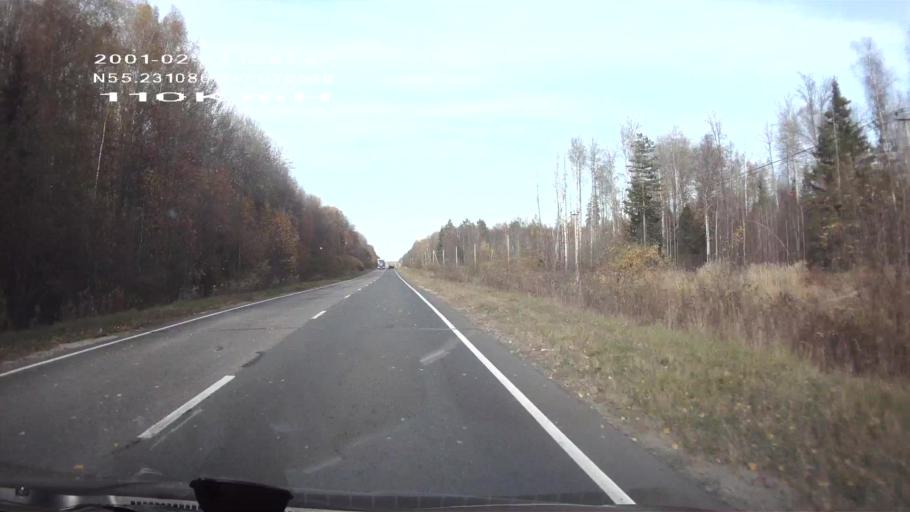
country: RU
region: Chuvashia
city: Buinsk
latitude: 55.2310
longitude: 47.0785
